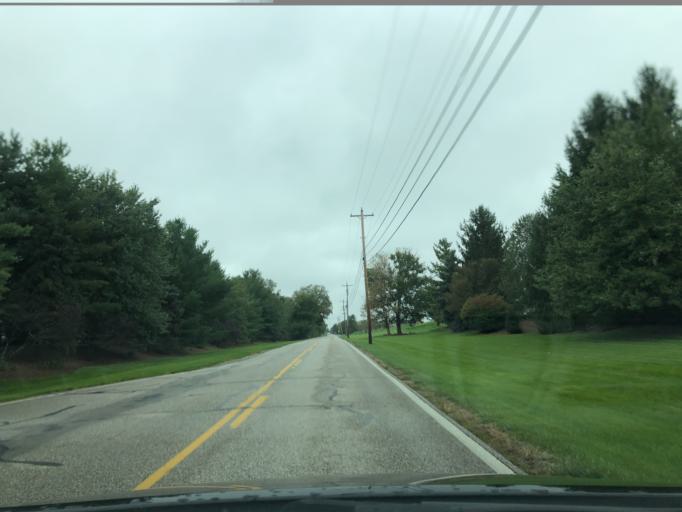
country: US
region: Ohio
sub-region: Hamilton County
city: Loveland
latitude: 39.2409
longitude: -84.2382
